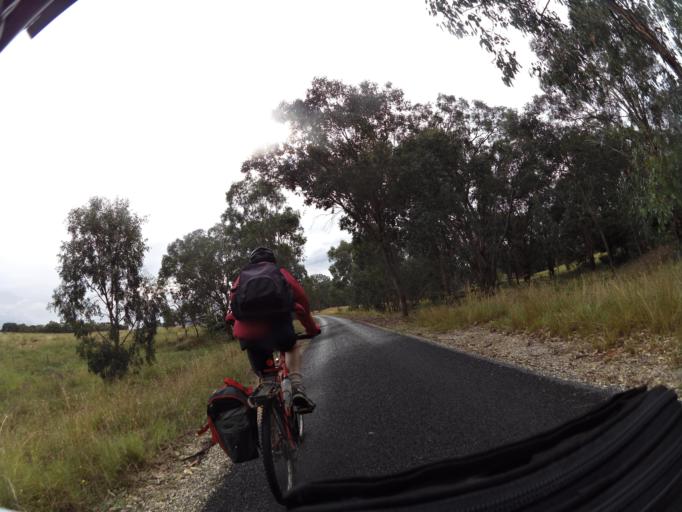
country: AU
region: New South Wales
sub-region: Albury Municipality
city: East Albury
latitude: -36.1417
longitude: 146.9948
